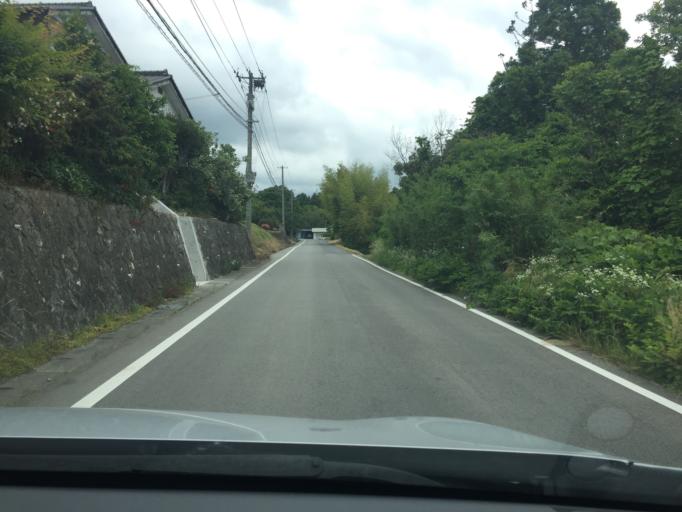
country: JP
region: Fukushima
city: Iwaki
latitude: 37.1147
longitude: 140.9041
